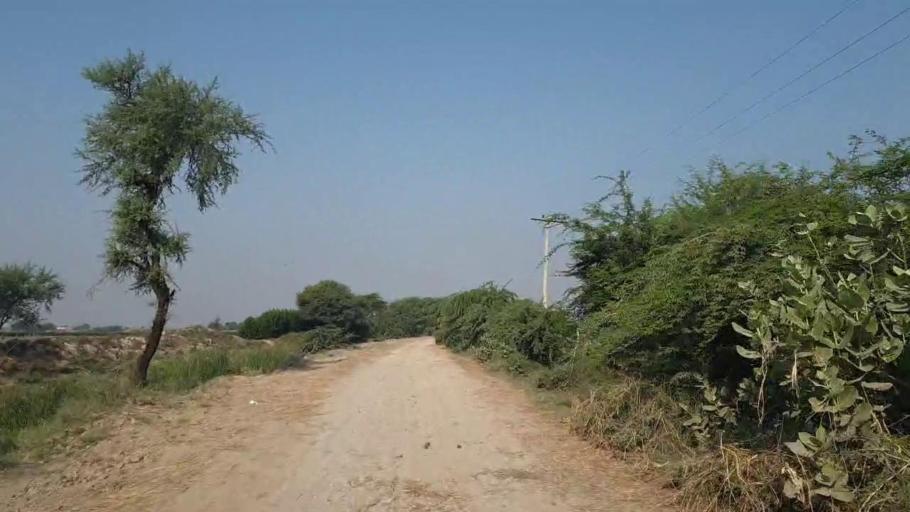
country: PK
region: Sindh
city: Matli
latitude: 24.9897
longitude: 68.6234
